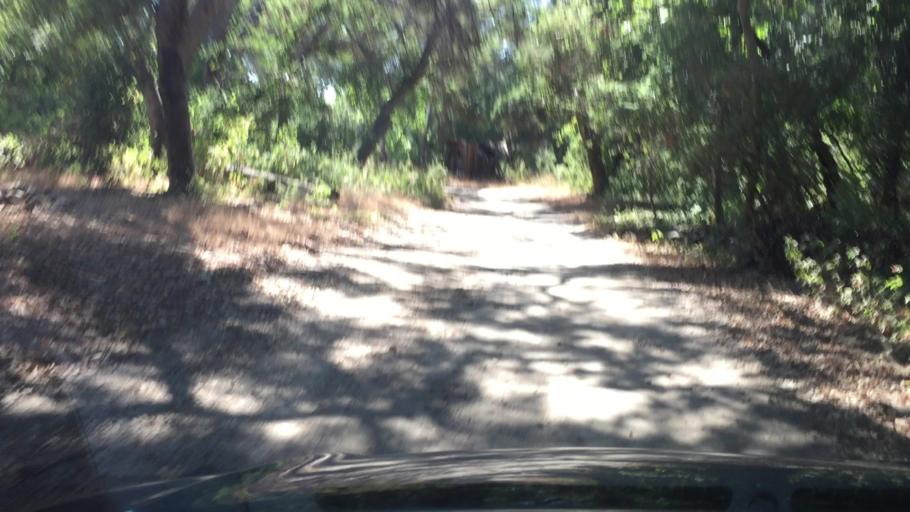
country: US
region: California
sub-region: San Diego County
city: Alpine
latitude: 32.7565
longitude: -116.7459
